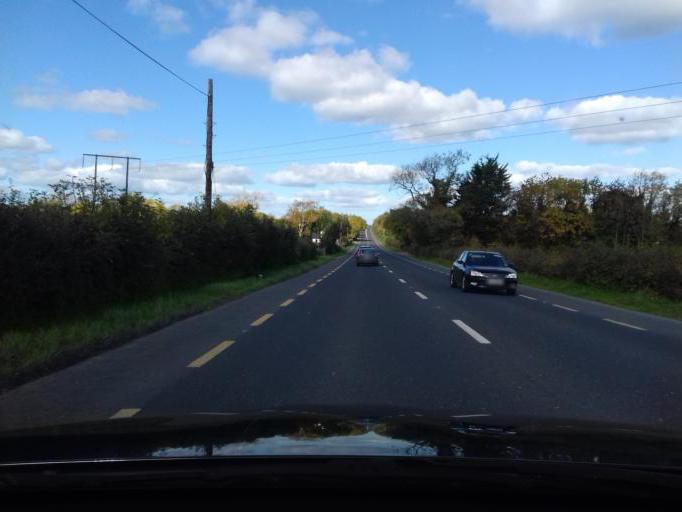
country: IE
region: Leinster
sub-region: An Mhi
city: Slane
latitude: 53.6704
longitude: -6.5330
